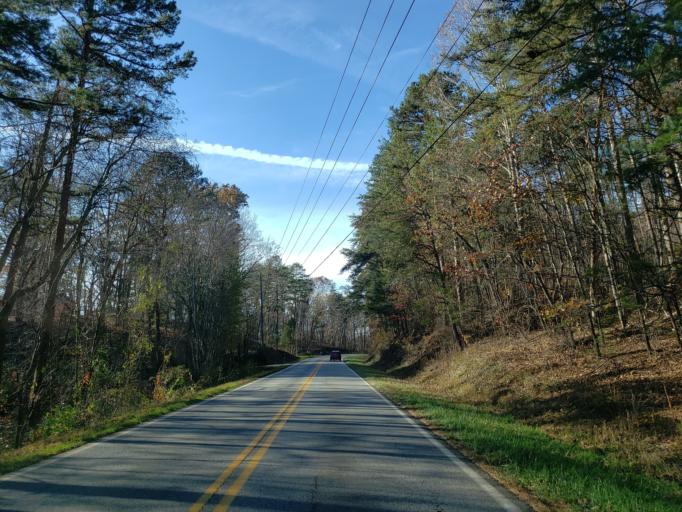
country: US
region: Georgia
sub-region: Lumpkin County
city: Dahlonega
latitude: 34.4525
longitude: -83.9953
